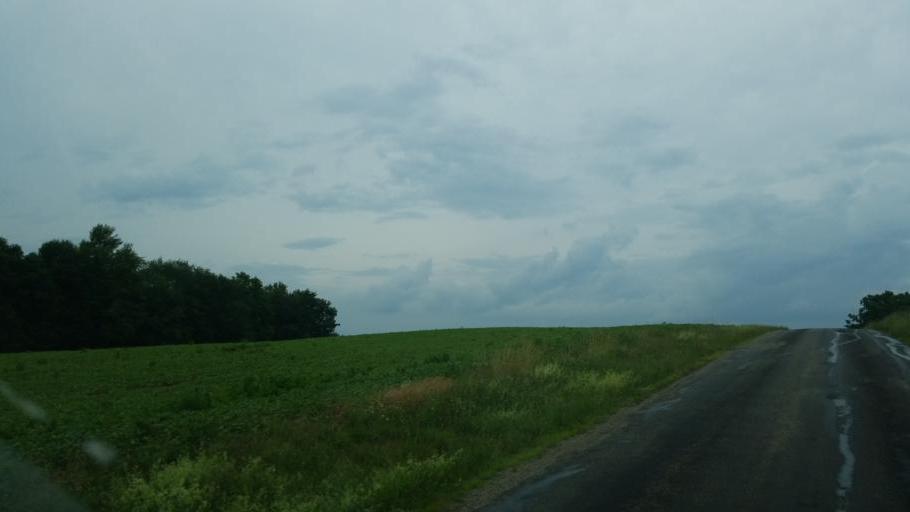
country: US
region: Ohio
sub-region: Sandusky County
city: Bellville
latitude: 40.5925
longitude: -82.5678
